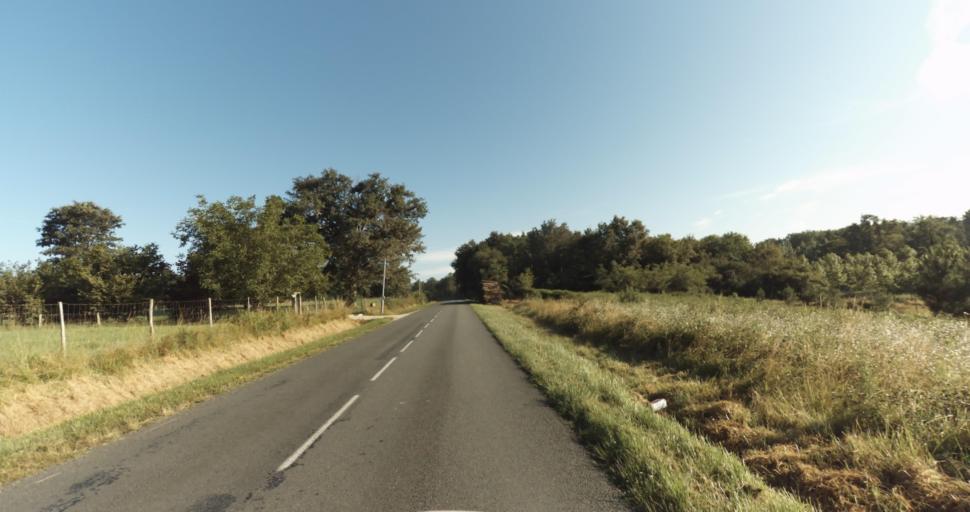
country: FR
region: Aquitaine
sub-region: Departement de la Gironde
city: Bazas
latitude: 44.4066
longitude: -0.2067
